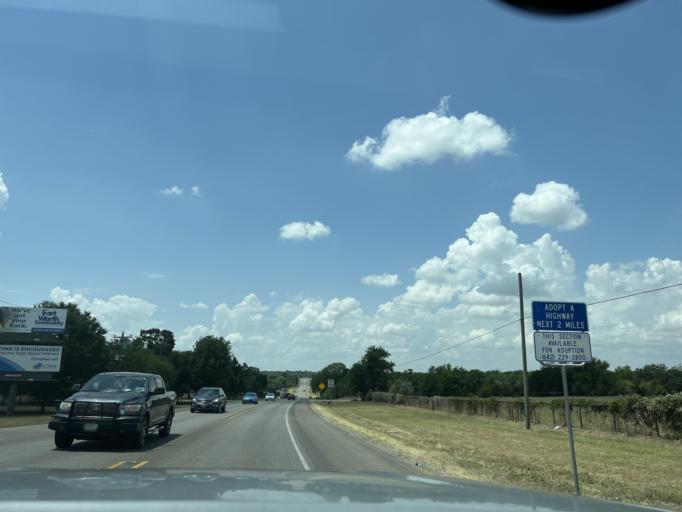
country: US
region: Texas
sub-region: Parker County
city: Weatherford
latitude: 32.8106
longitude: -97.7789
